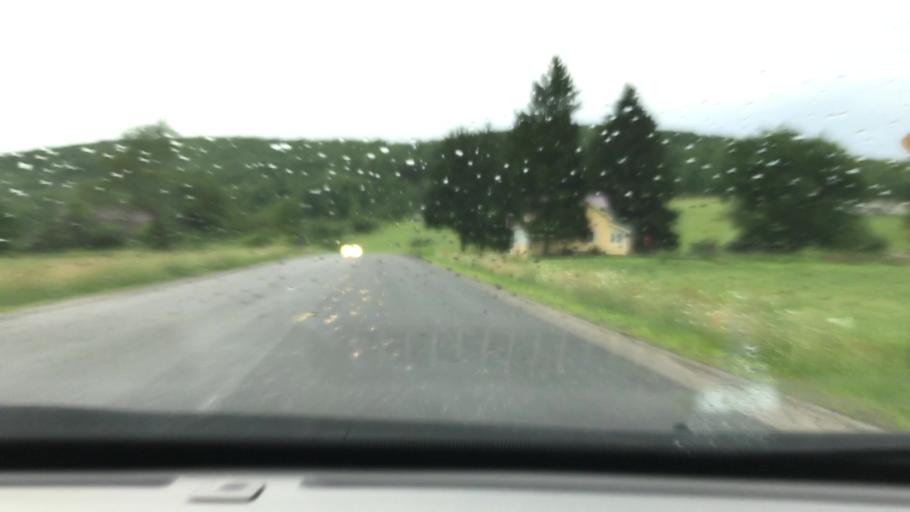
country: US
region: New York
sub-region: Cattaraugus County
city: Little Valley
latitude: 42.3178
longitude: -78.6625
